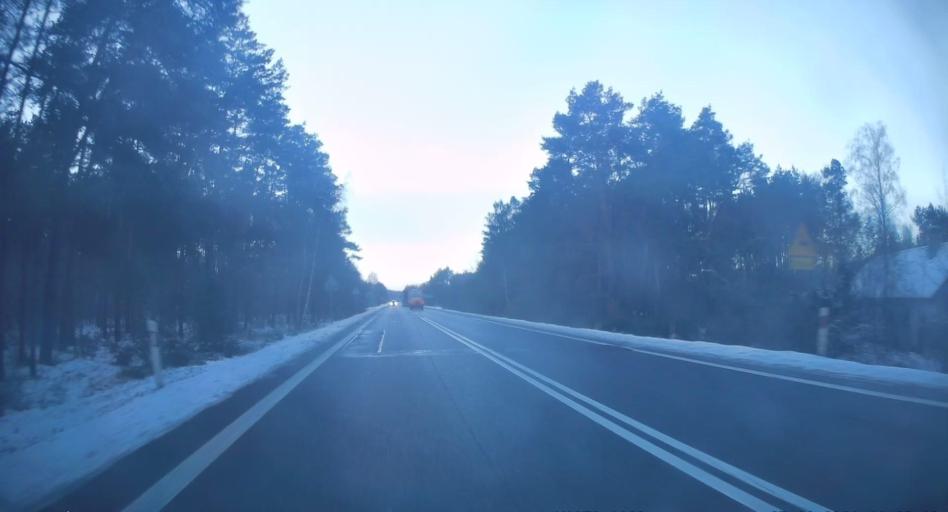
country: PL
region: Swietokrzyskie
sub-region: Powiat konecki
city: Ruda Maleniecka
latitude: 51.1268
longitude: 20.2557
